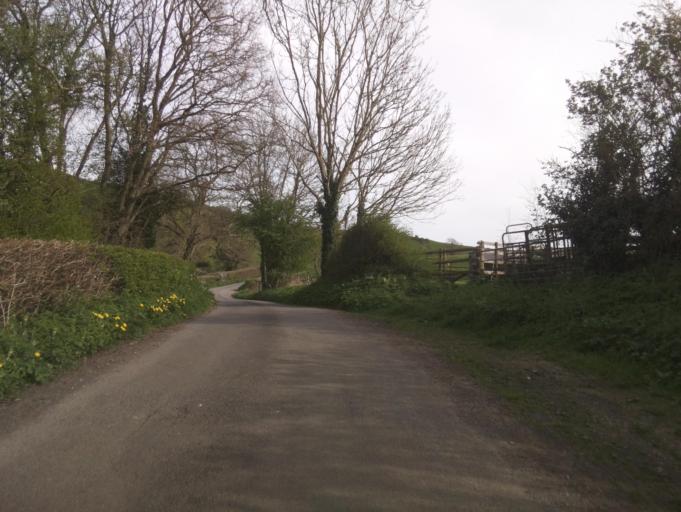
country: GB
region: England
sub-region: Somerset
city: Milborne Port
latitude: 50.9750
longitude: -2.4935
